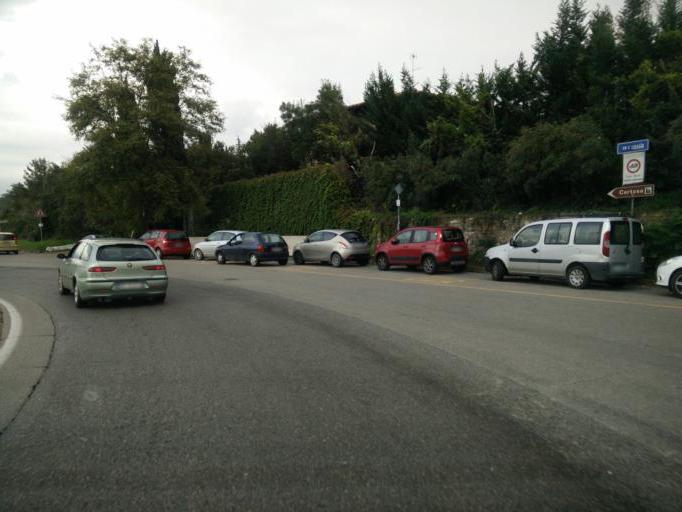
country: IT
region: Tuscany
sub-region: Province of Florence
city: Tavarnuzze
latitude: 43.7199
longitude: 11.2233
